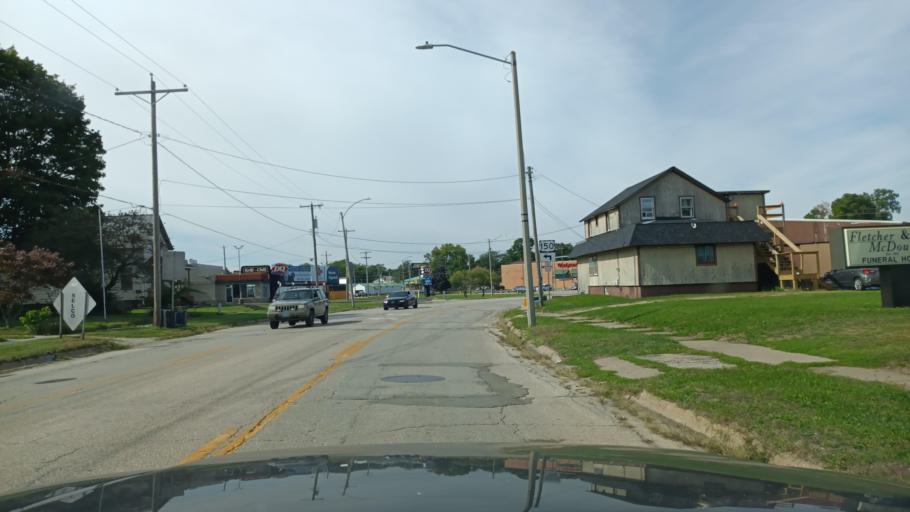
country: US
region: Illinois
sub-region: Knox County
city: Galesburg
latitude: 40.9463
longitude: -90.3533
